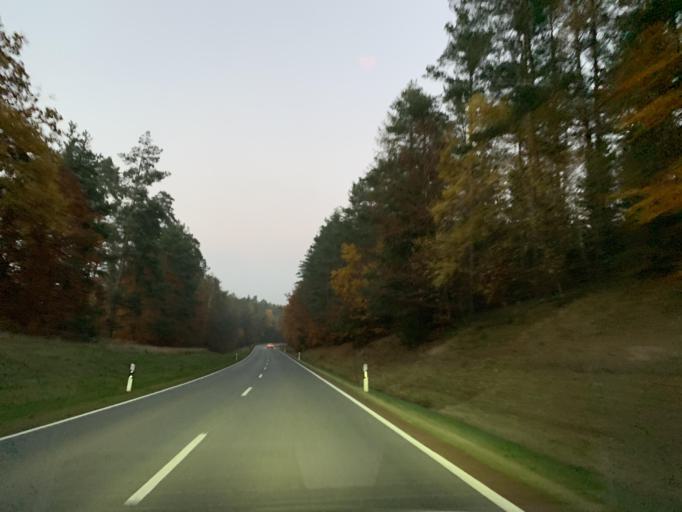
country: DE
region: Bavaria
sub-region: Upper Palatinate
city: Brunn
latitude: 49.2257
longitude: 12.1543
